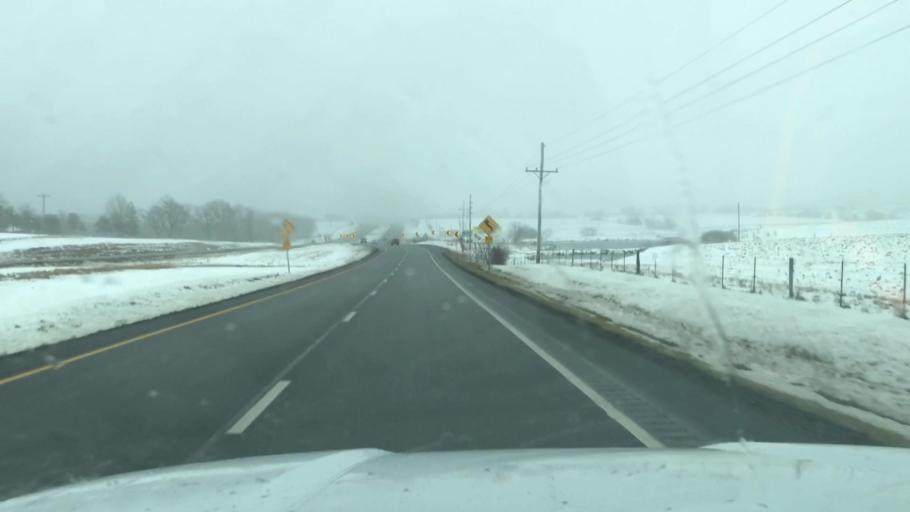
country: US
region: Missouri
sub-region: Clinton County
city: Cameron
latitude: 39.7539
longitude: -94.2706
